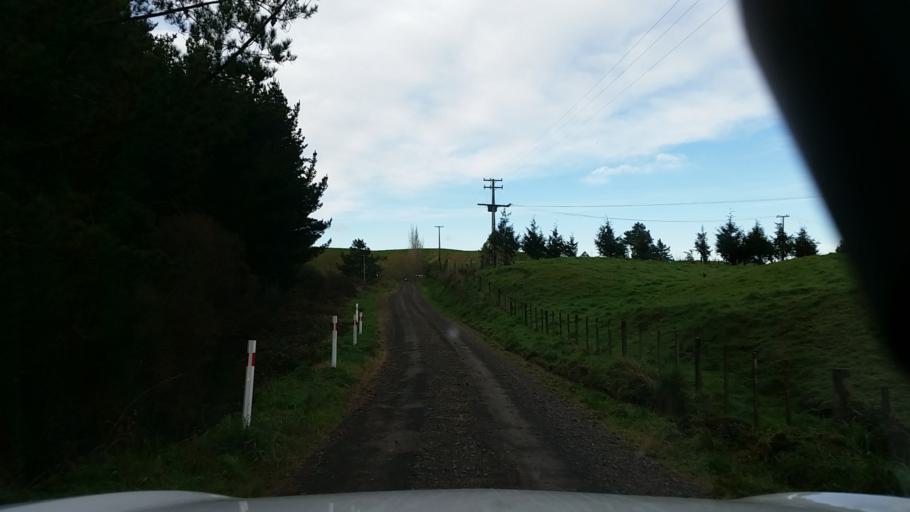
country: NZ
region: Bay of Plenty
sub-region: Rotorua District
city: Rotorua
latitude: -38.2704
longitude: 176.1562
